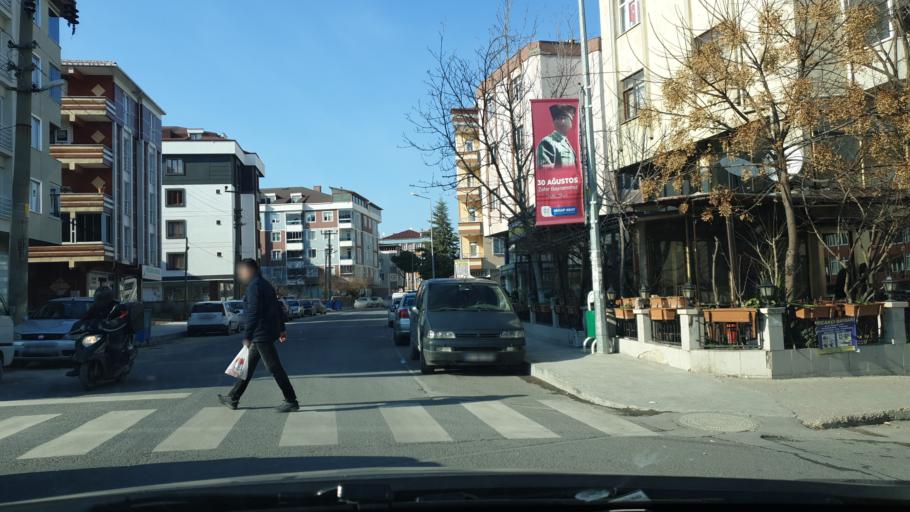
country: TR
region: Tekirdag
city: Cerkezkoey
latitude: 41.2849
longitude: 27.9938
